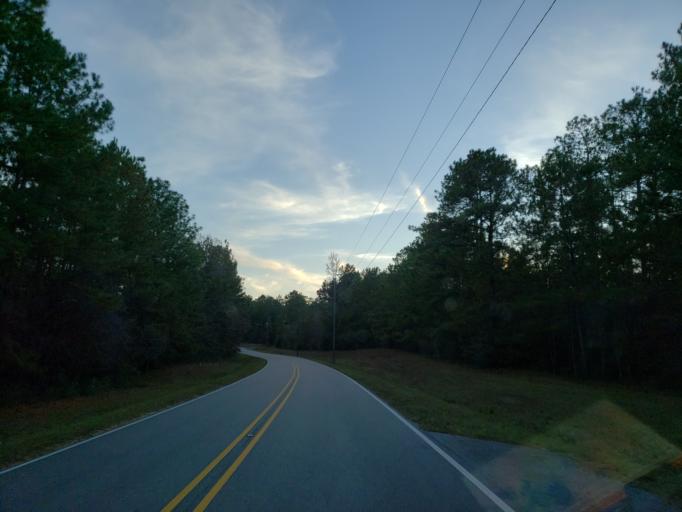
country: US
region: Mississippi
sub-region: Forrest County
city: Hattiesburg
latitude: 31.2618
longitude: -89.3134
